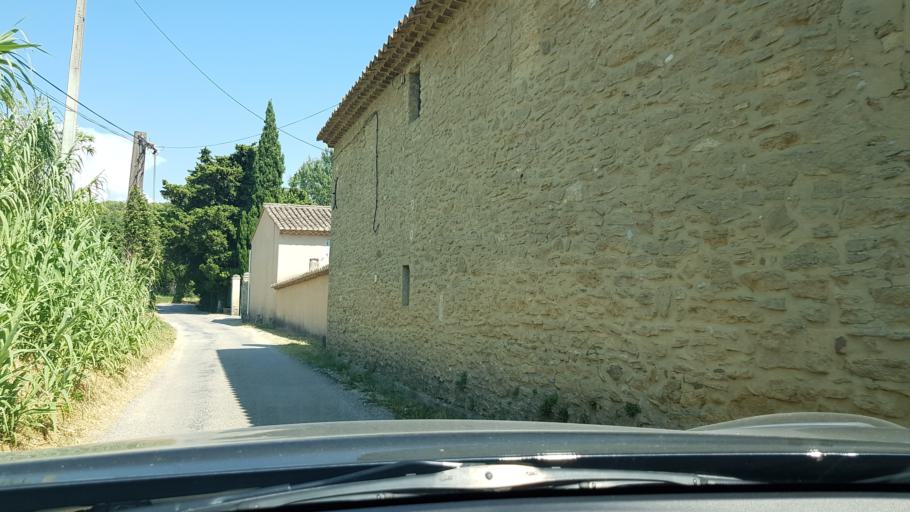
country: FR
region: Provence-Alpes-Cote d'Azur
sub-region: Departement du Vaucluse
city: Vacqueyras
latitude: 44.1147
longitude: 4.9807
